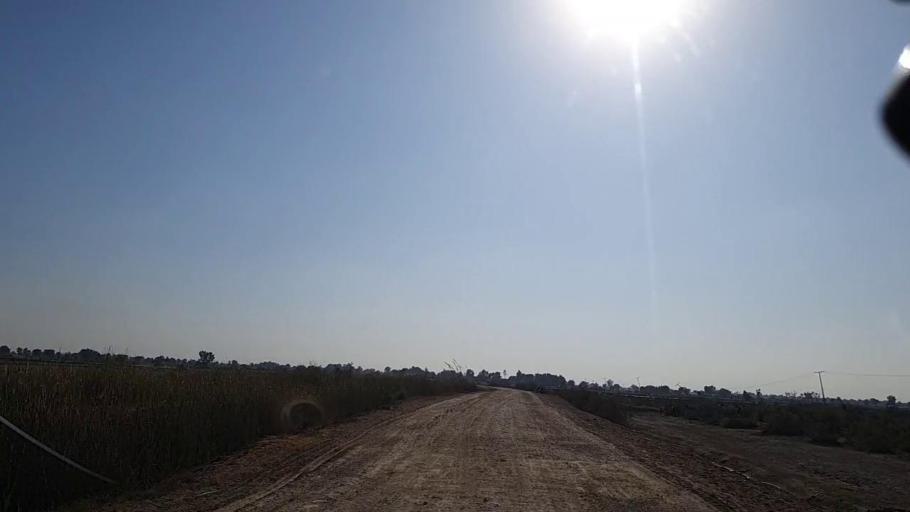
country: PK
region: Sindh
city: Khanpur
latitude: 27.7949
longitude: 69.3719
